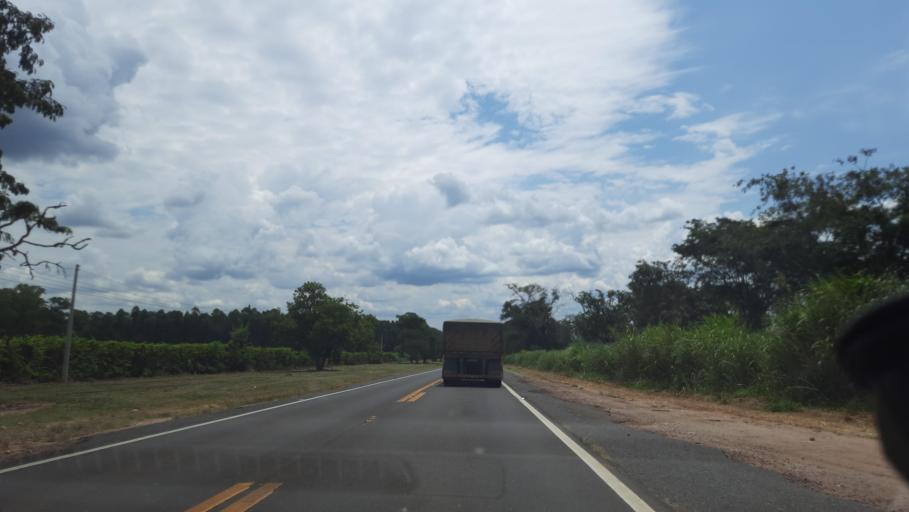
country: BR
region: Sao Paulo
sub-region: Mococa
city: Mococa
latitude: -21.5101
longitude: -47.0438
